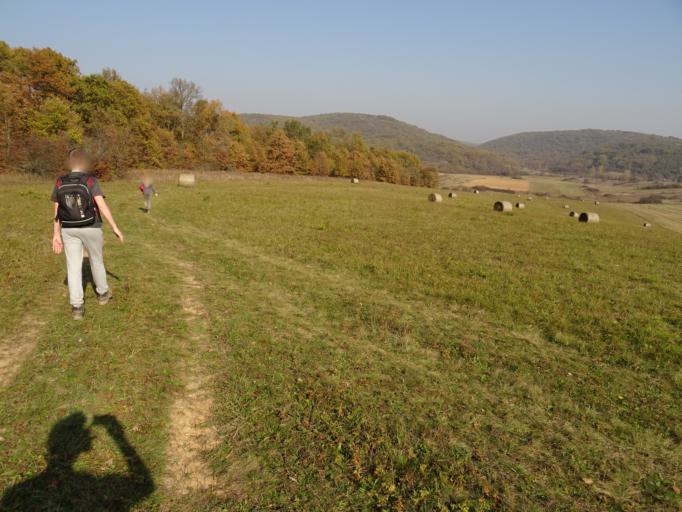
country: HU
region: Borsod-Abauj-Zemplen
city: Putnok
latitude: 48.4667
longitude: 20.4800
